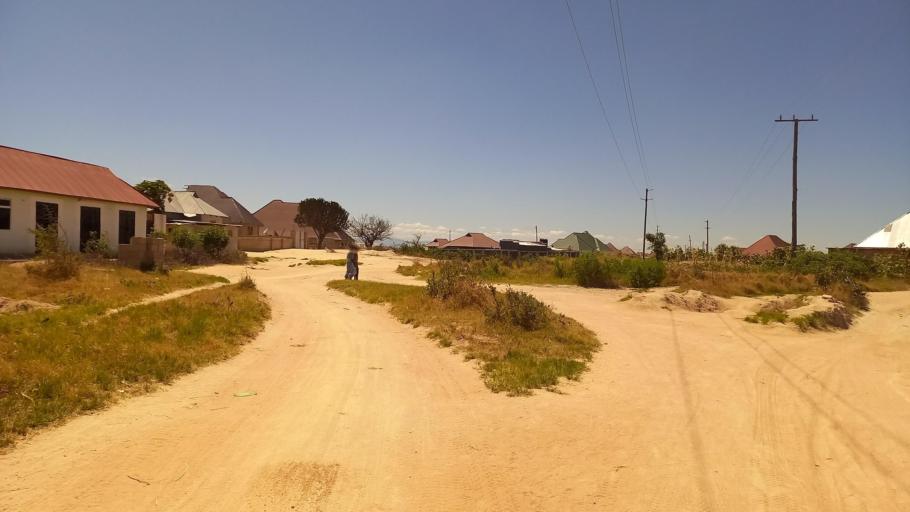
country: TZ
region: Dodoma
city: Dodoma
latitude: -6.1356
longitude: 35.7100
